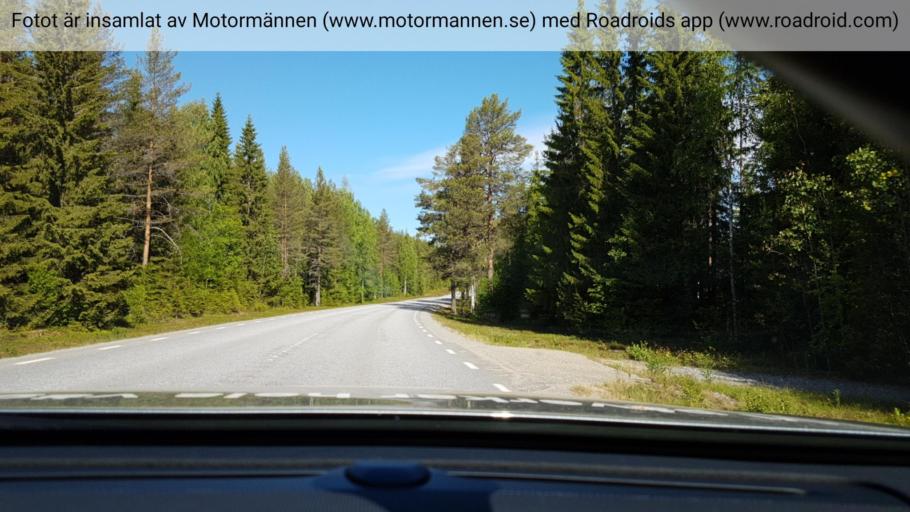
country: SE
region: Vaesterbotten
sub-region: Bjurholms Kommun
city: Bjurholm
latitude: 63.9367
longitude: 18.9364
